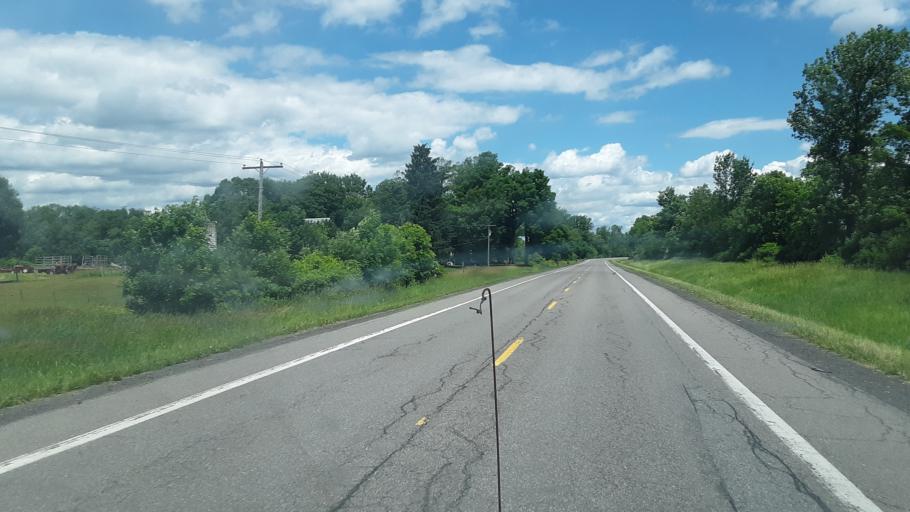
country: US
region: New York
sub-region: Madison County
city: Oneida
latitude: 43.1815
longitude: -75.6413
